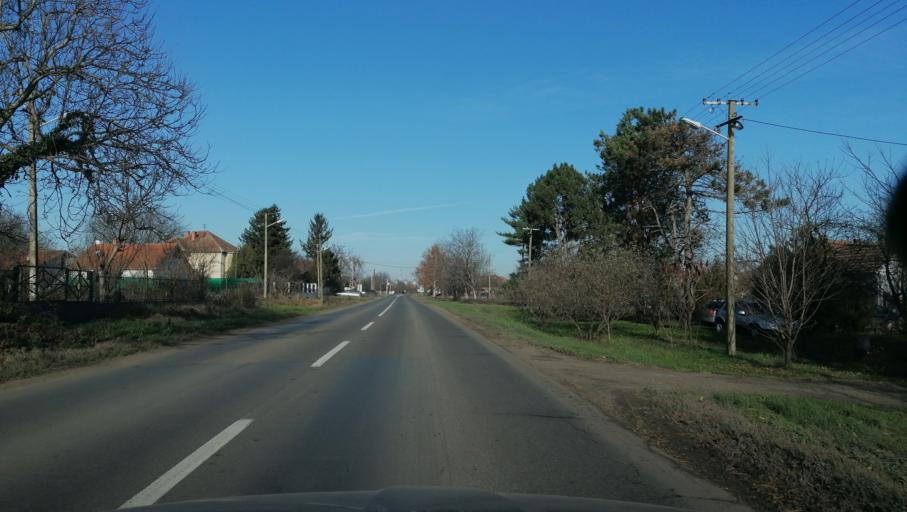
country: RS
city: Centa
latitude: 45.1179
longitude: 20.3863
